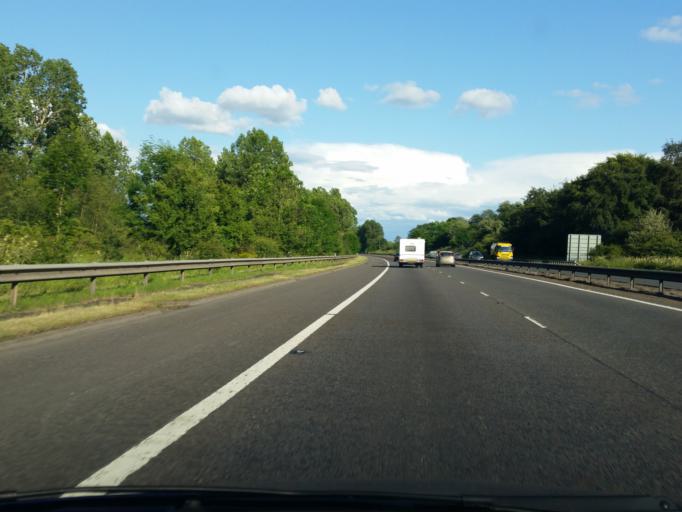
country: GB
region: Scotland
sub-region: North Lanarkshire
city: Motherwell
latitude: 55.7685
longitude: -4.0034
